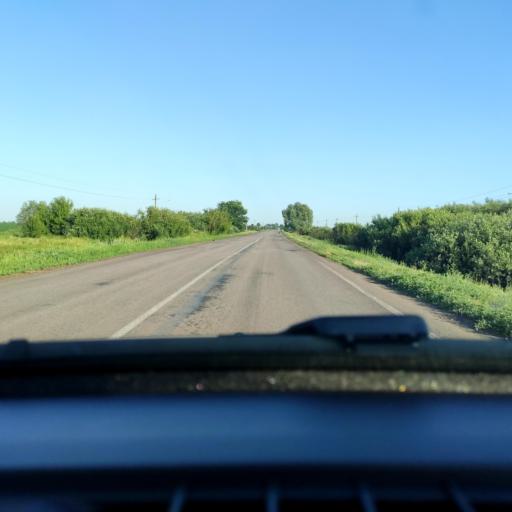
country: RU
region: Voronezj
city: Kashirskoye
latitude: 51.4888
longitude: 39.8515
